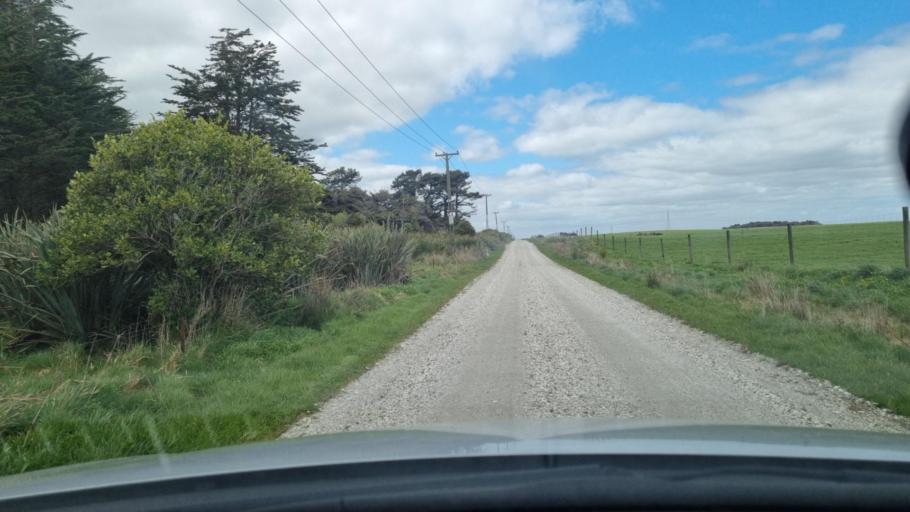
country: NZ
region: Southland
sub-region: Invercargill City
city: Invercargill
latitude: -46.4427
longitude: 168.4254
